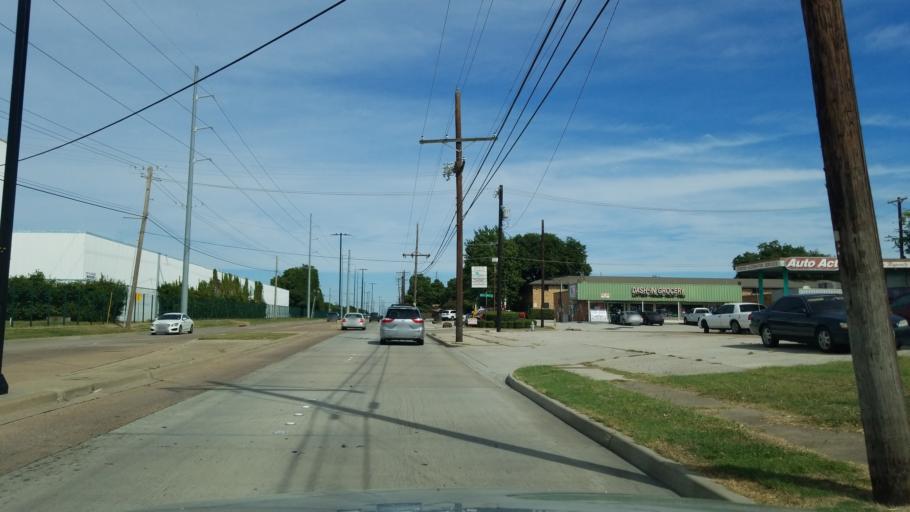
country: US
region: Texas
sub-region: Dallas County
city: Garland
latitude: 32.9013
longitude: -96.6655
